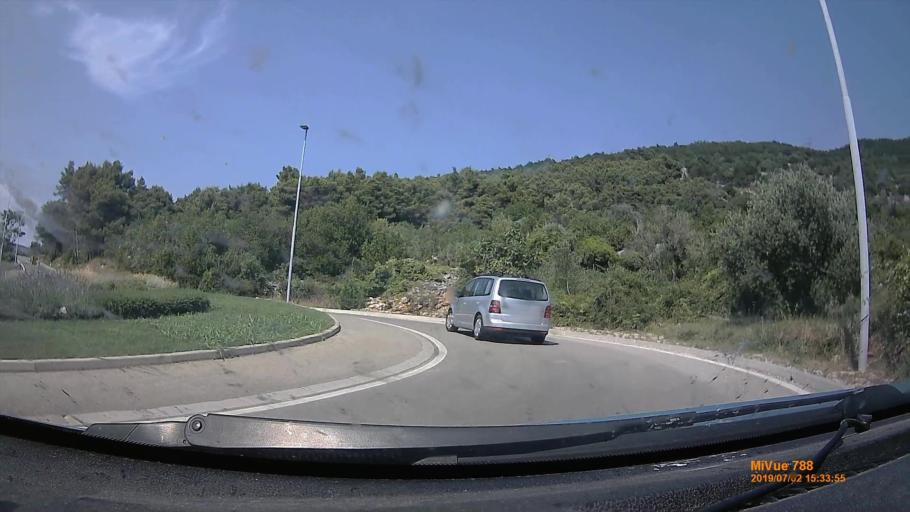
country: HR
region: Primorsko-Goranska
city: Cres
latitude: 44.9631
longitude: 14.4132
